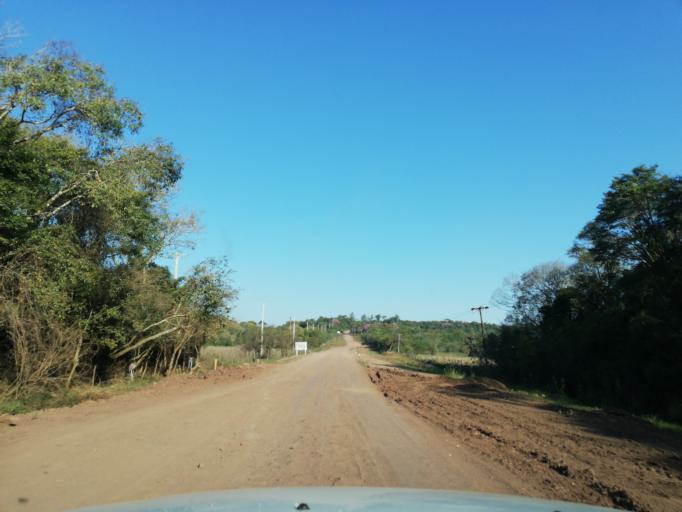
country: AR
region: Misiones
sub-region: Departamento de Candelaria
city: Candelaria
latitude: -27.5354
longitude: -55.7169
